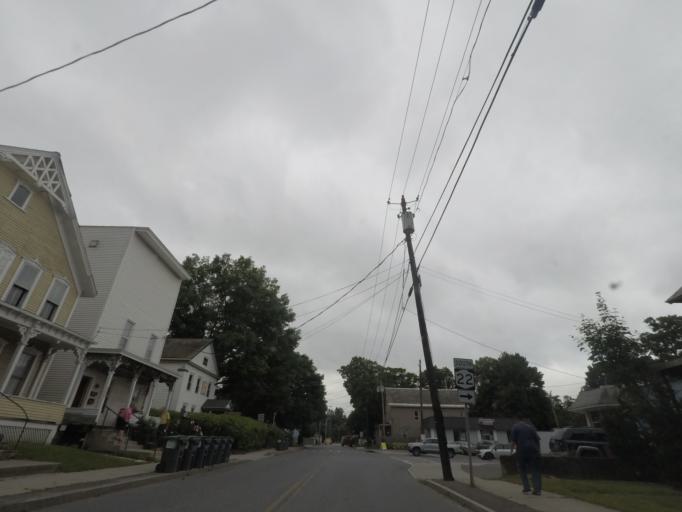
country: US
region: New York
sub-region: Rensselaer County
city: Hoosick Falls
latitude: 42.8971
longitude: -73.3516
